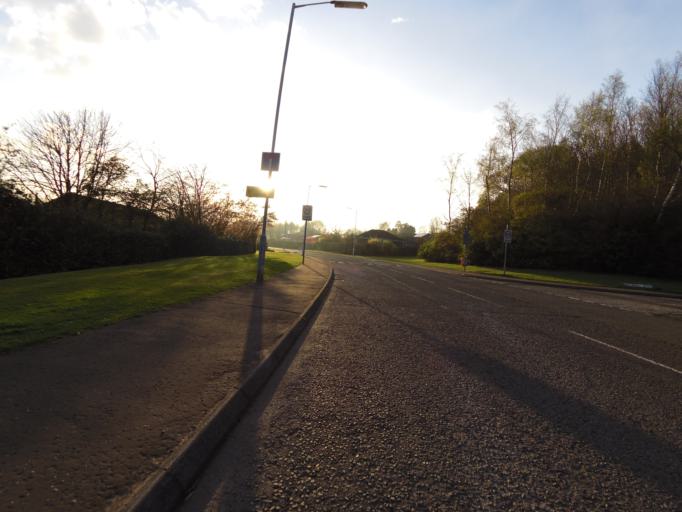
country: GB
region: Scotland
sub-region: Fife
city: Leslie
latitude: 56.2091
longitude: -3.1982
